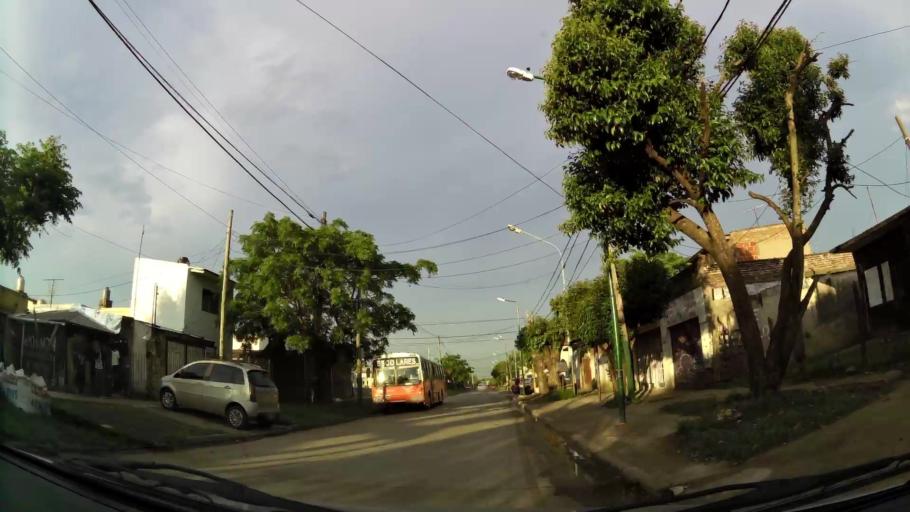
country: AR
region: Buenos Aires
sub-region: Partido de Almirante Brown
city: Adrogue
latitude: -34.7743
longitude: -58.3479
